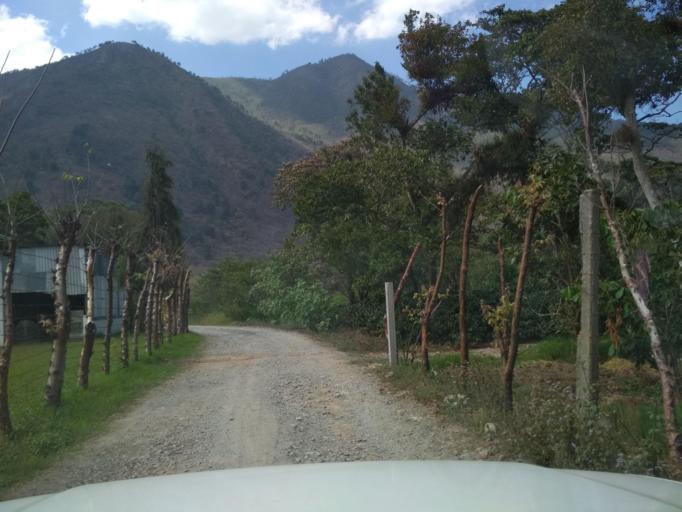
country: MX
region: Veracruz
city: Jalapilla
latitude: 18.7981
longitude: -97.1028
